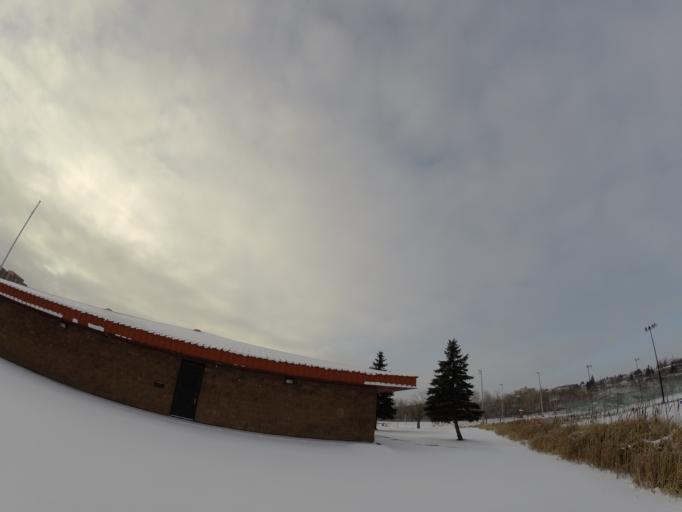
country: CA
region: Ontario
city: Greater Sudbury
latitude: 46.4692
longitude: -80.9998
